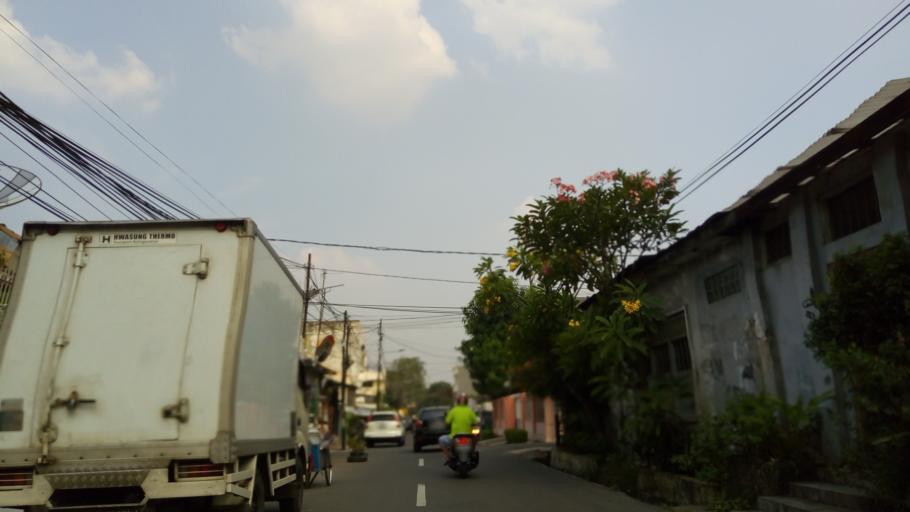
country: ID
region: Jakarta Raya
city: Jakarta
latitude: -6.1795
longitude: 106.8439
